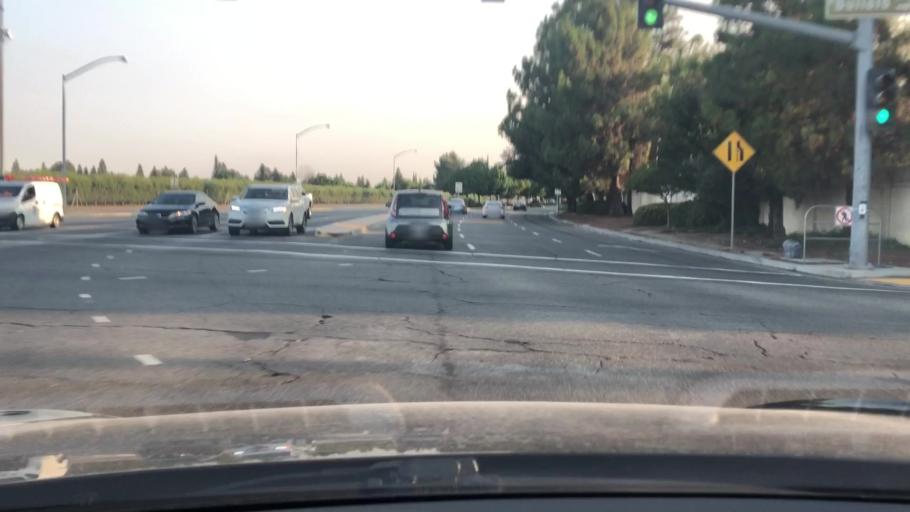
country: US
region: California
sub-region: Fresno County
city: Clovis
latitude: 36.8231
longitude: -119.7291
